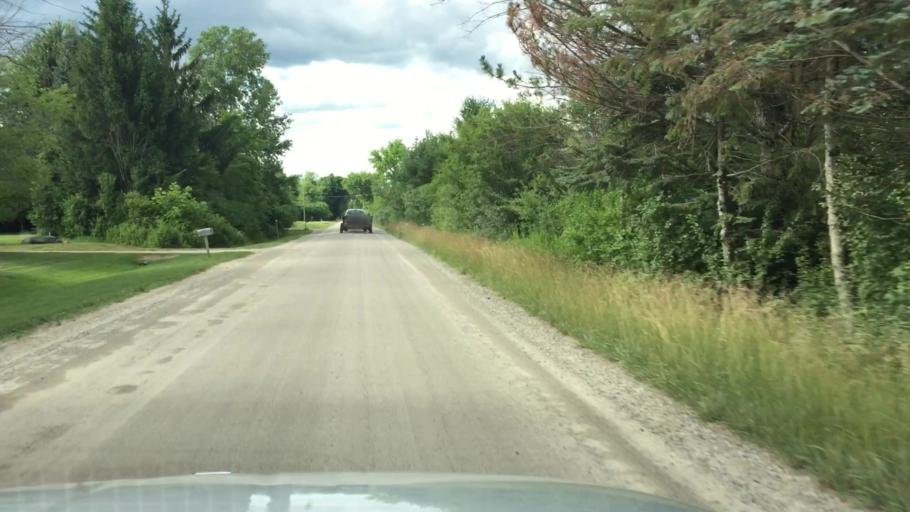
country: US
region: Michigan
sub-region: Saint Clair County
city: Yale
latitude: 43.1394
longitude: -82.8188
